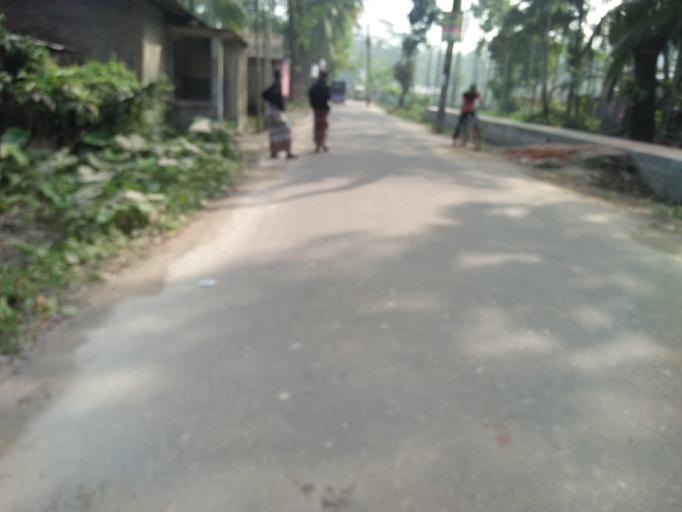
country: BD
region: Barisal
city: Bhola
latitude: 22.6799
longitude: 90.6383
